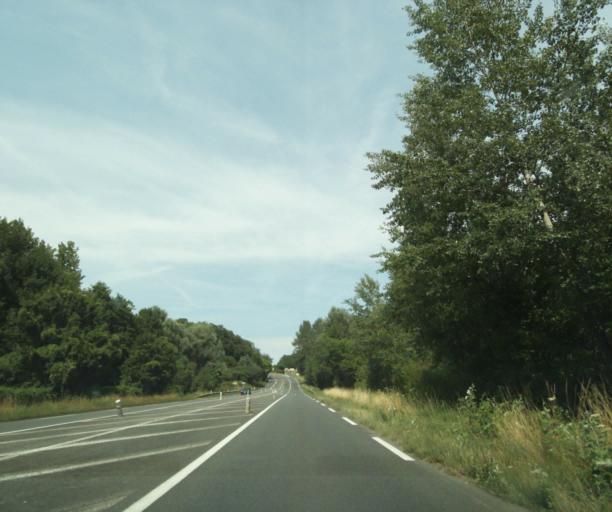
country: FR
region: Centre
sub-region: Departement d'Indre-et-Loire
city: Sainte-Maure-de-Touraine
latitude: 47.1417
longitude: 0.6438
